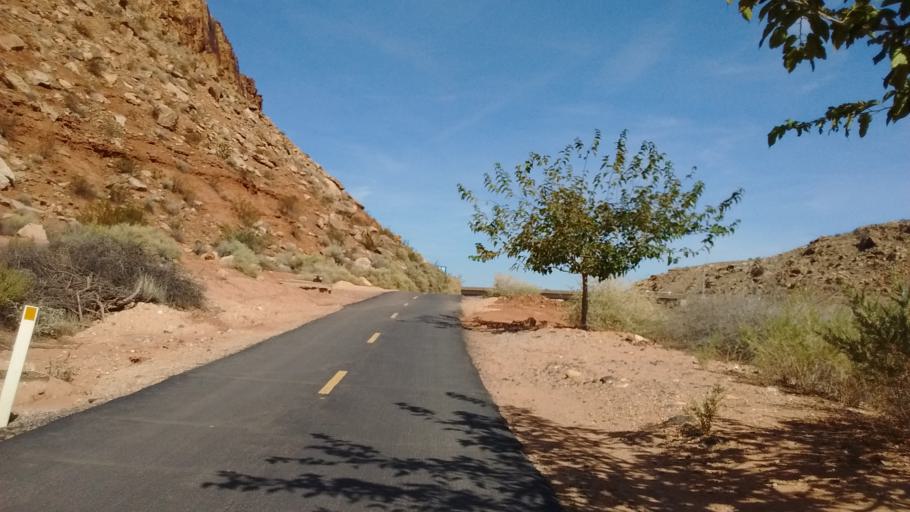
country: US
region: Utah
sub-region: Washington County
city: Saint George
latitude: 37.0678
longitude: -113.5871
